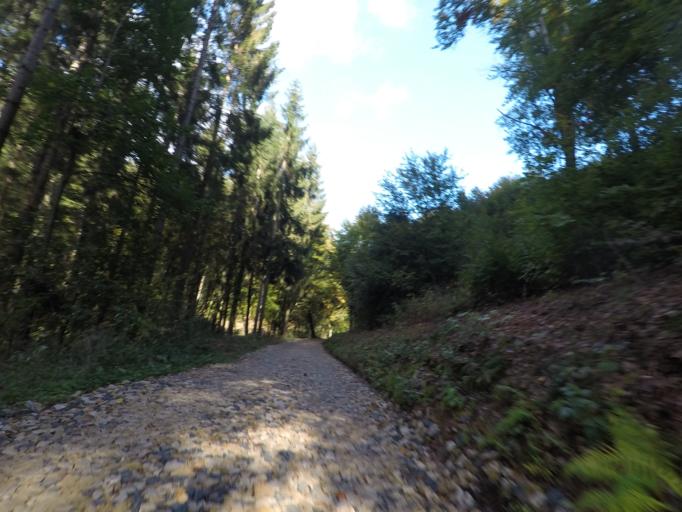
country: LU
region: Luxembourg
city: Itzig
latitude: 49.6071
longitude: 6.1821
